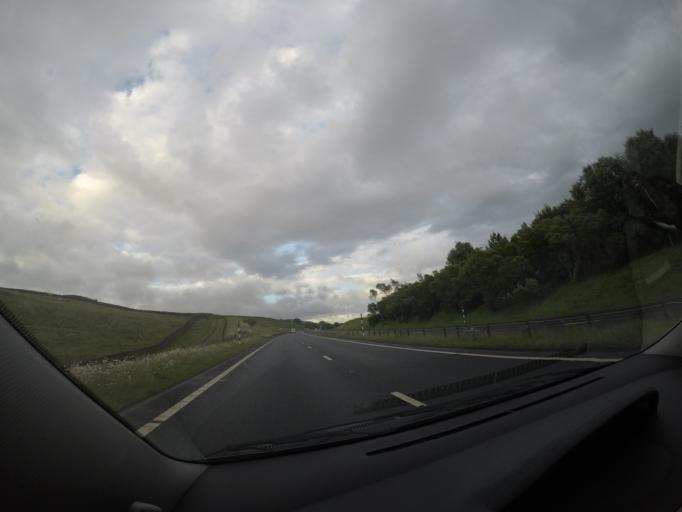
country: GB
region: England
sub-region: Cumbria
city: Kirkby Stephen
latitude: 54.5302
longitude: -2.2531
